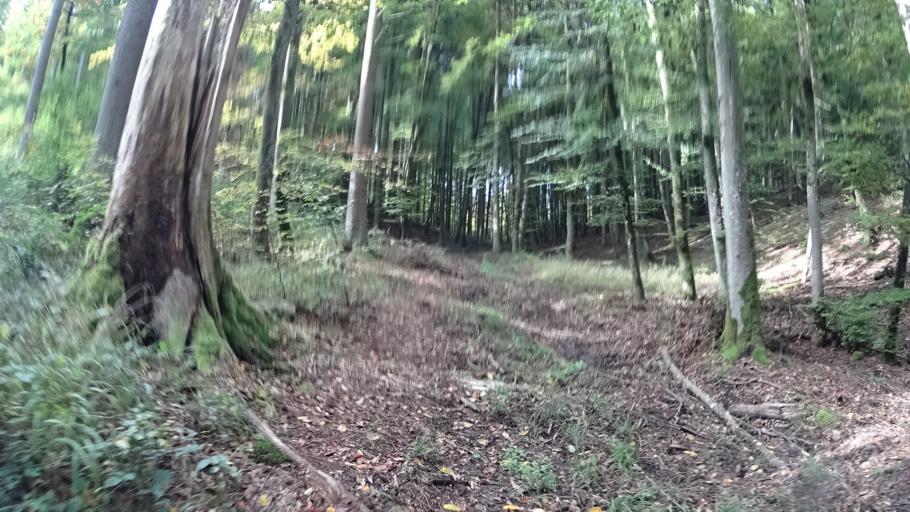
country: DE
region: Bavaria
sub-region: Upper Bavaria
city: Bohmfeld
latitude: 48.8920
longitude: 11.3368
